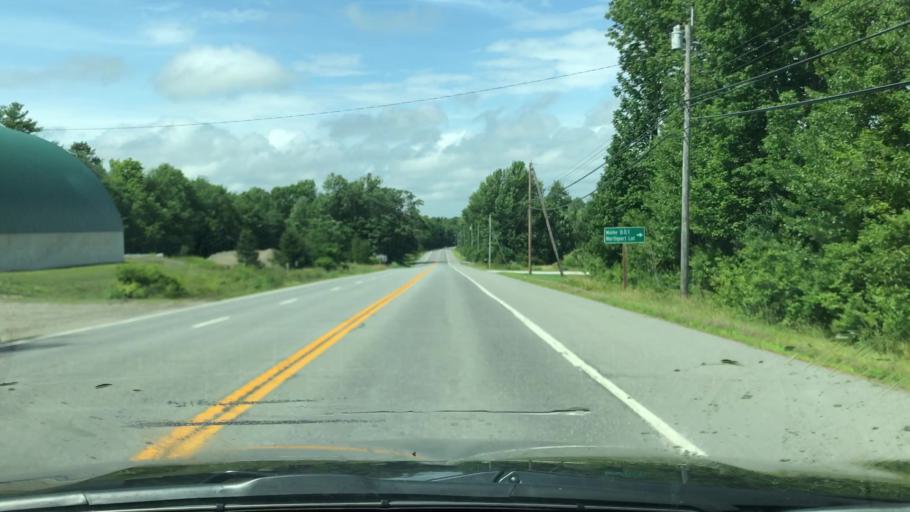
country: US
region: Maine
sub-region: Waldo County
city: Northport
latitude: 44.3664
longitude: -68.9795
